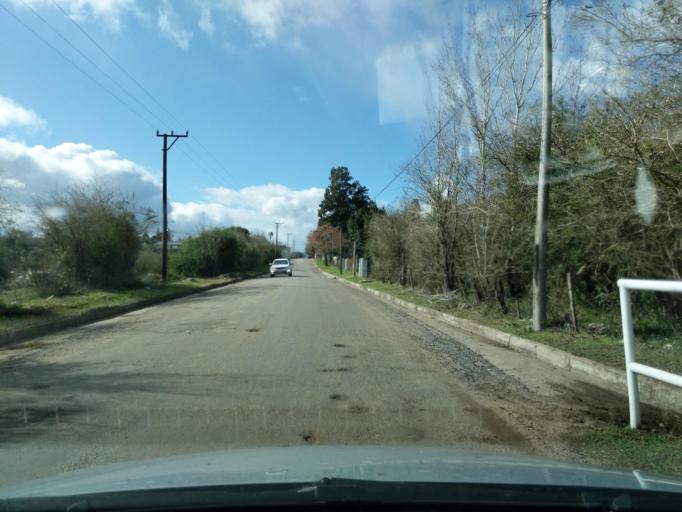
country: UY
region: Florida
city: Florida
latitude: -34.1080
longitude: -56.2190
